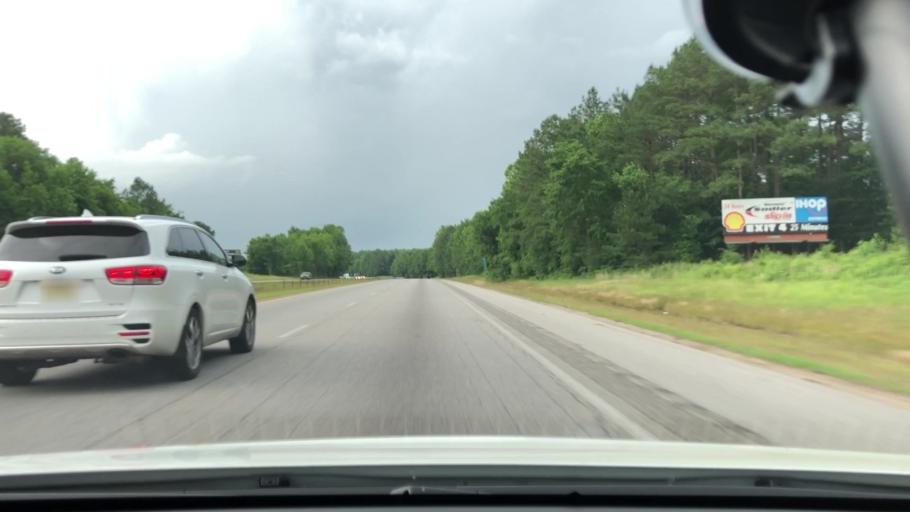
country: US
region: North Carolina
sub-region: Halifax County
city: Enfield
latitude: 36.2430
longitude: -77.7322
